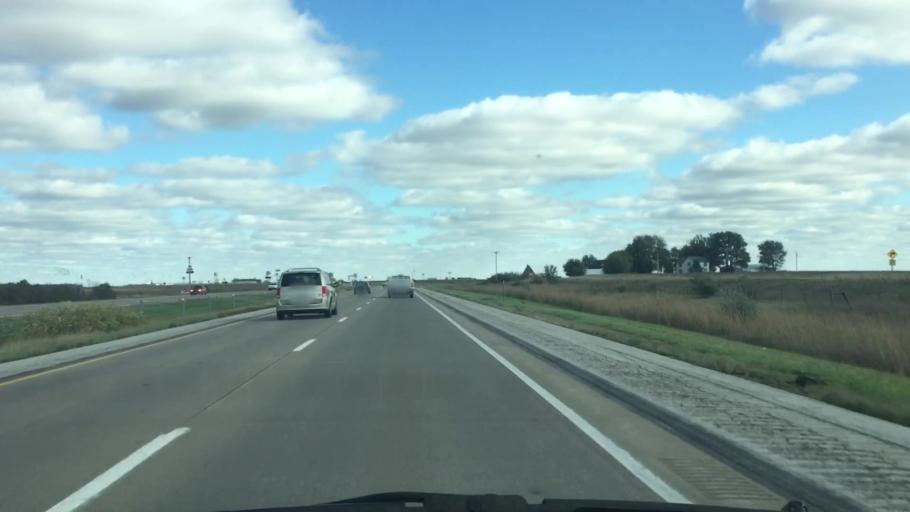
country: US
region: Iowa
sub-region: Scott County
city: Walcott
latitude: 41.6221
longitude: -90.8057
